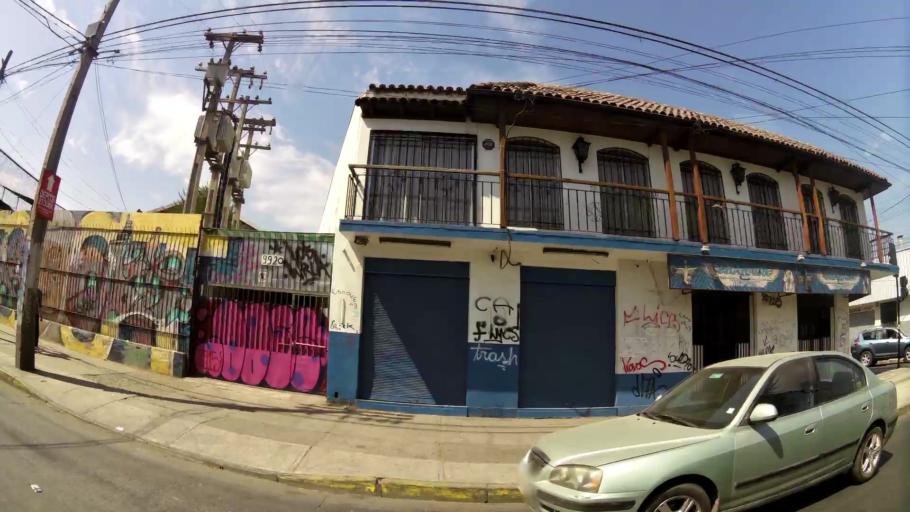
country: CL
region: Santiago Metropolitan
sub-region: Provincia de Maipo
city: San Bernardo
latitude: -33.5510
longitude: -70.6724
